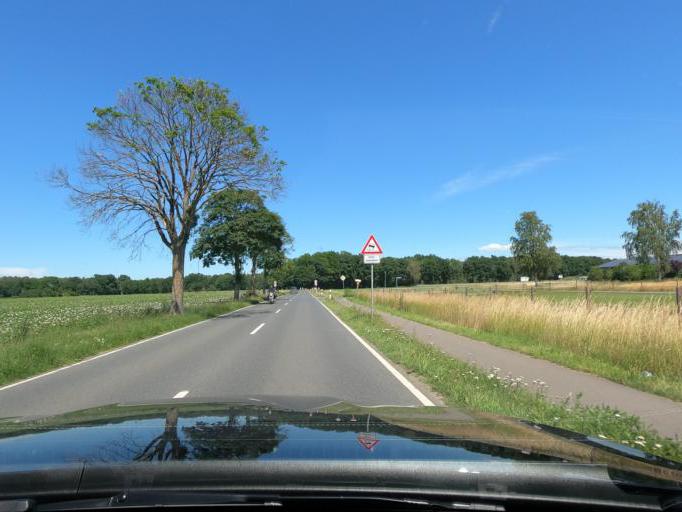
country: DE
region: Lower Saxony
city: Eicklingen
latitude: 52.5619
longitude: 10.1864
